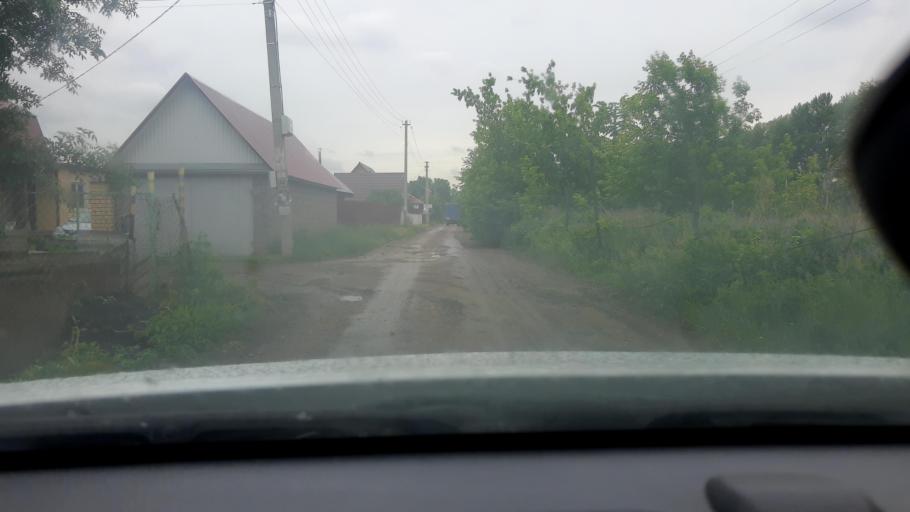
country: RU
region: Bashkortostan
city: Kabakovo
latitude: 54.4715
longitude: 55.9409
